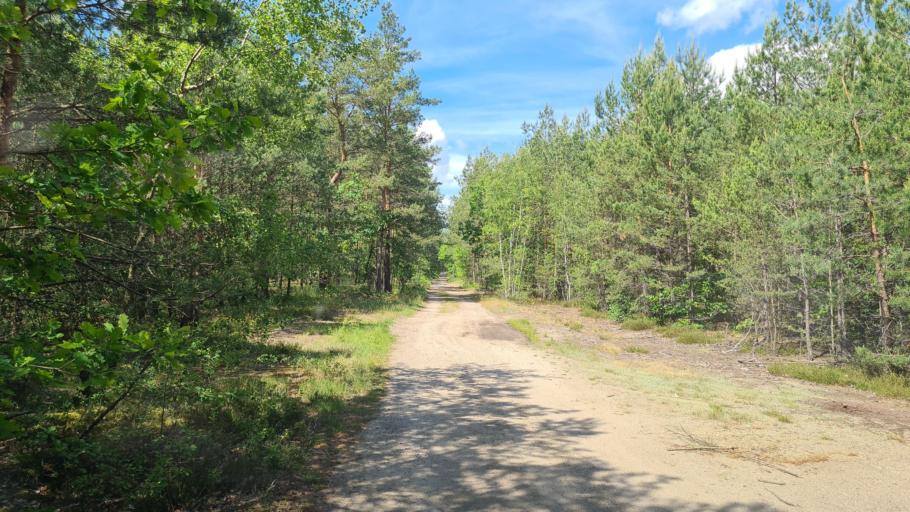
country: DE
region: Brandenburg
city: Sallgast
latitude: 51.5906
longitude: 13.8325
